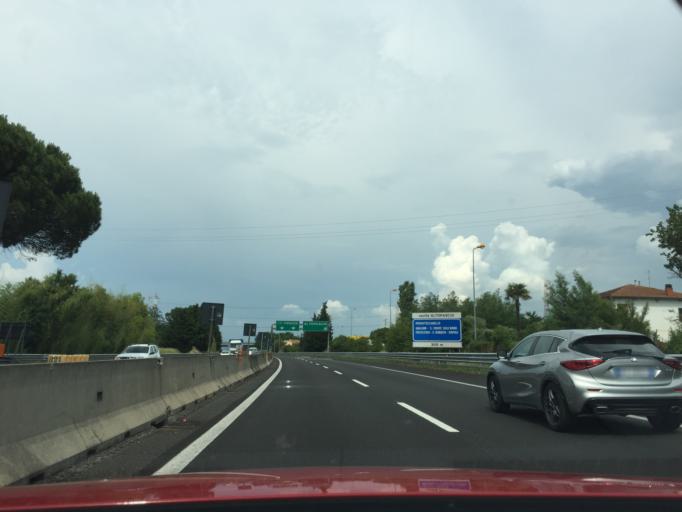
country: IT
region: Tuscany
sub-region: Provincia di Lucca
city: Altopascio
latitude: 43.8199
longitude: 10.6835
